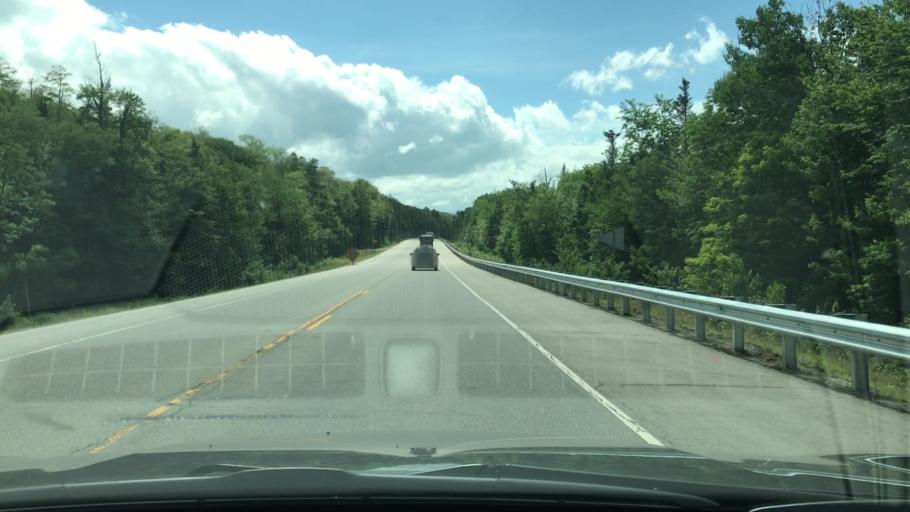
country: US
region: New Hampshire
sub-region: Coos County
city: Gorham
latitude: 44.3695
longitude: -71.3029
